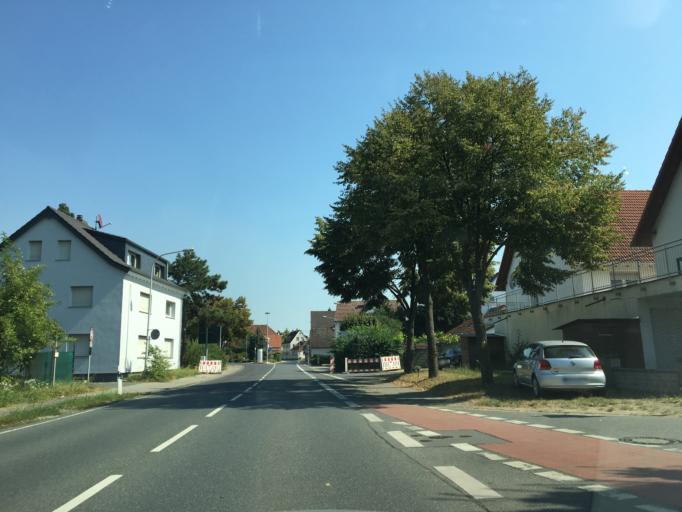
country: DE
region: Hesse
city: Griesheim
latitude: 49.8591
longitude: 8.5495
